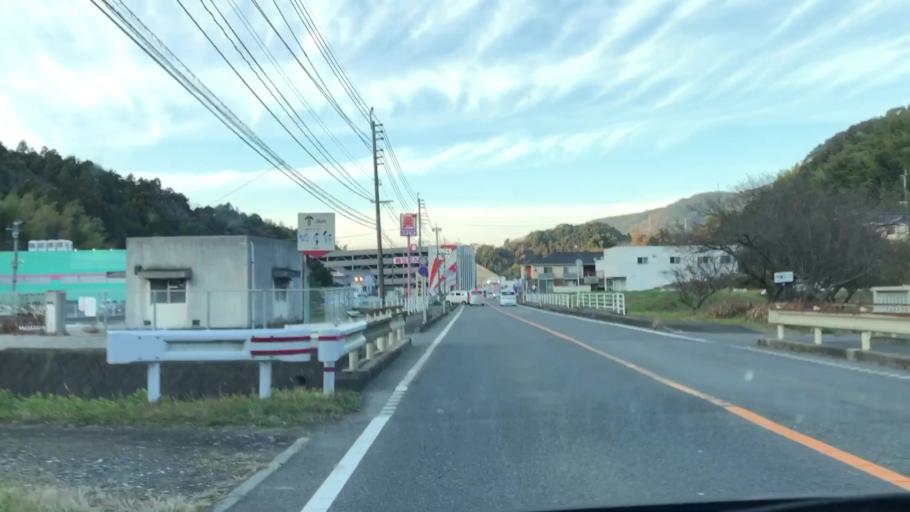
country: JP
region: Kumamoto
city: Minamata
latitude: 32.2207
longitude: 130.4382
